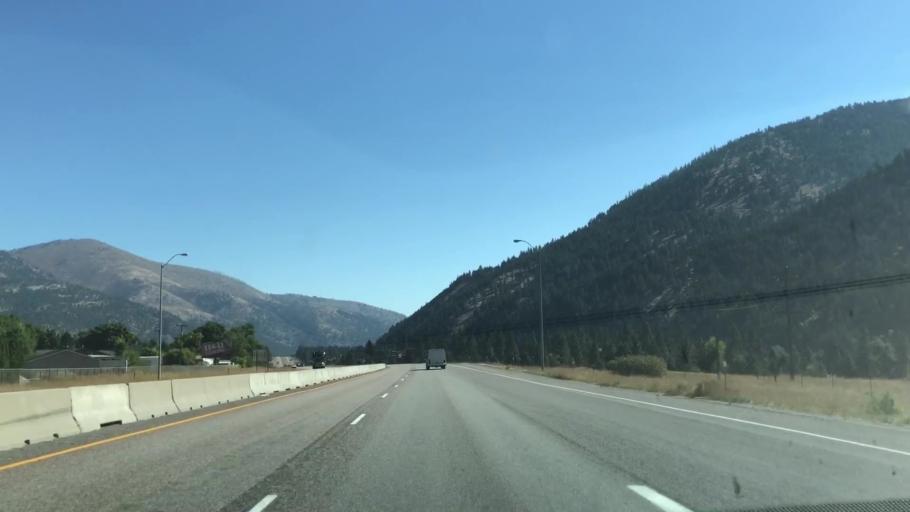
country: US
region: Montana
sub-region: Missoula County
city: East Missoula
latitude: 46.8674
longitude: -113.9468
